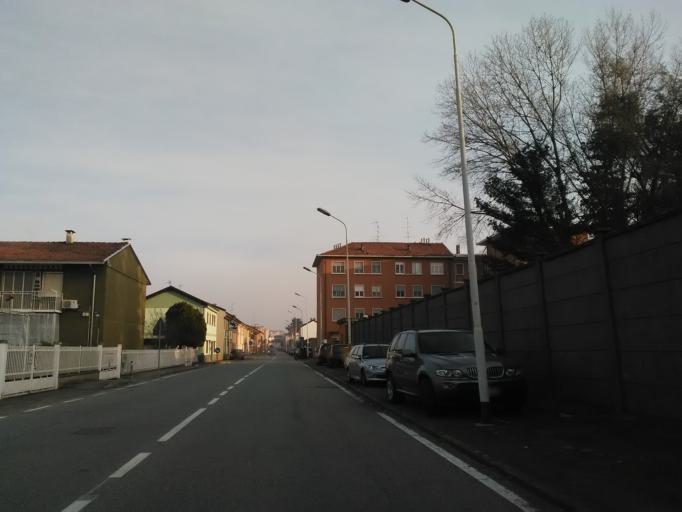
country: IT
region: Piedmont
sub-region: Provincia di Vercelli
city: Vercelli
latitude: 45.3301
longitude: 8.4047
